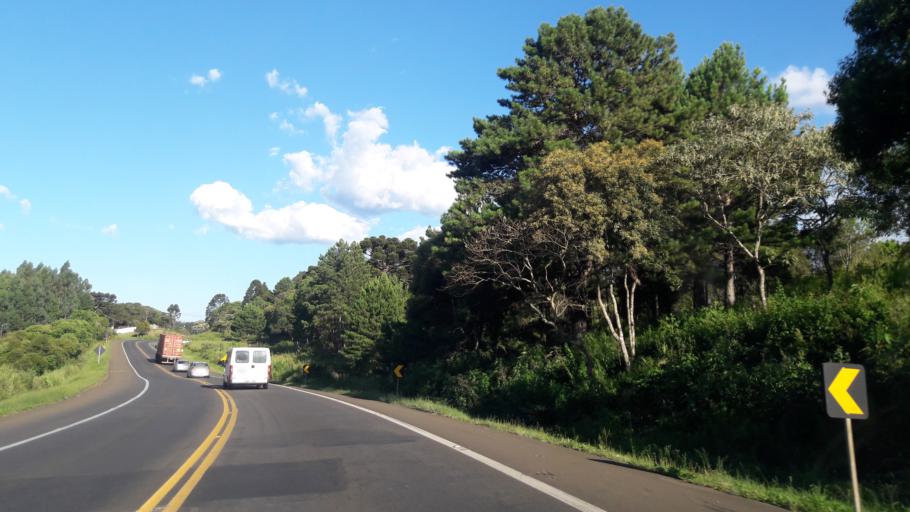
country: BR
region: Parana
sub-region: Guarapuava
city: Guarapuava
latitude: -25.3679
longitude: -51.3392
